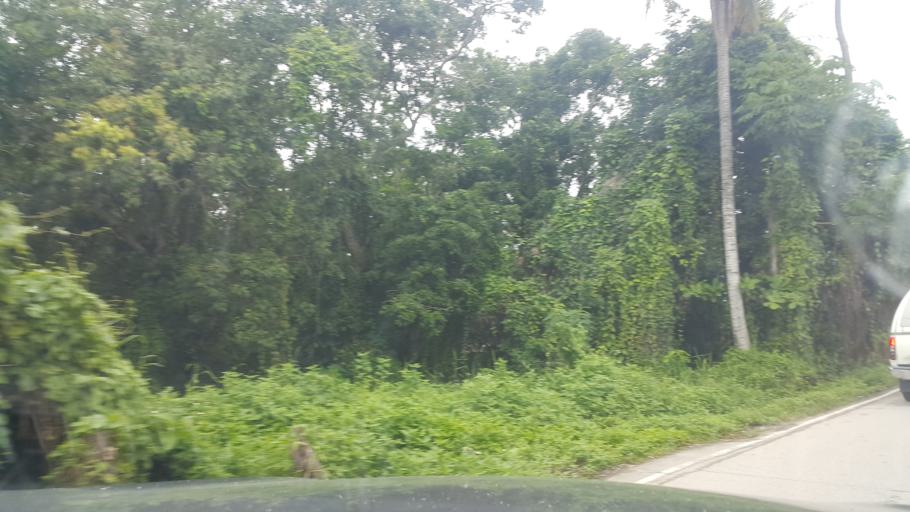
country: TH
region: Chiang Mai
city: San Sai
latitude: 18.8531
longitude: 99.0422
